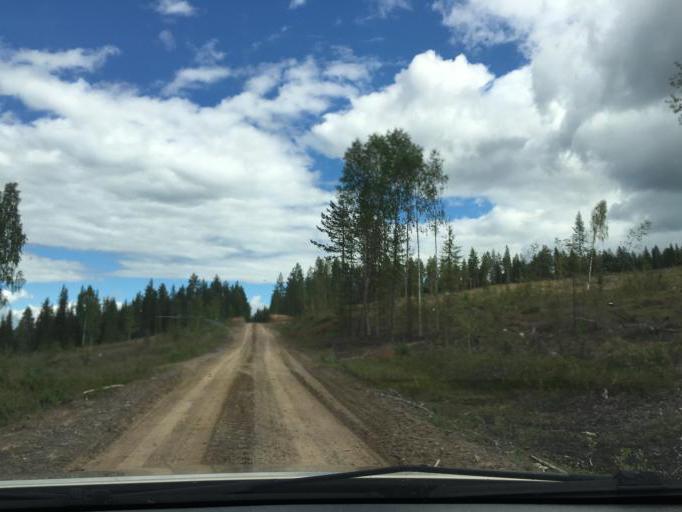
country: SE
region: Norrbotten
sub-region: Overkalix Kommun
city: OEverkalix
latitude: 66.1451
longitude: 22.7896
